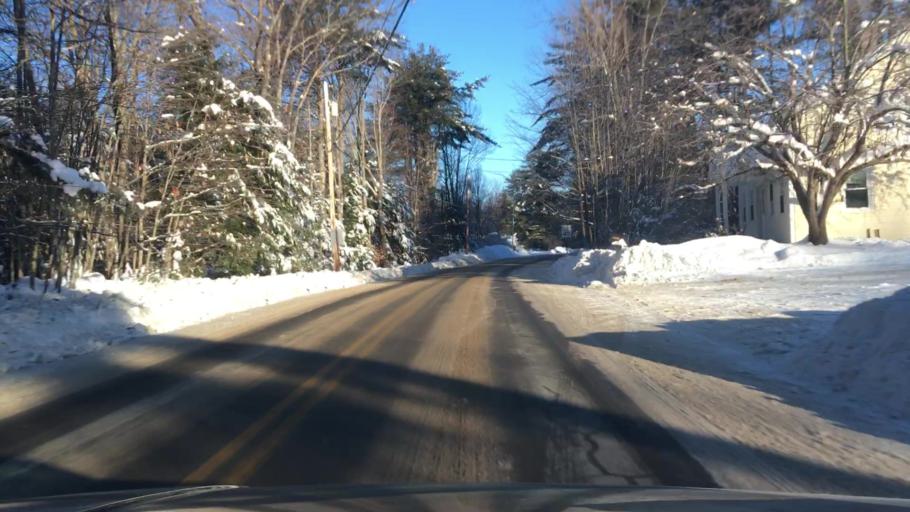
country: US
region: Maine
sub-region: Oxford County
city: Lovell
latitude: 44.1336
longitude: -70.9785
